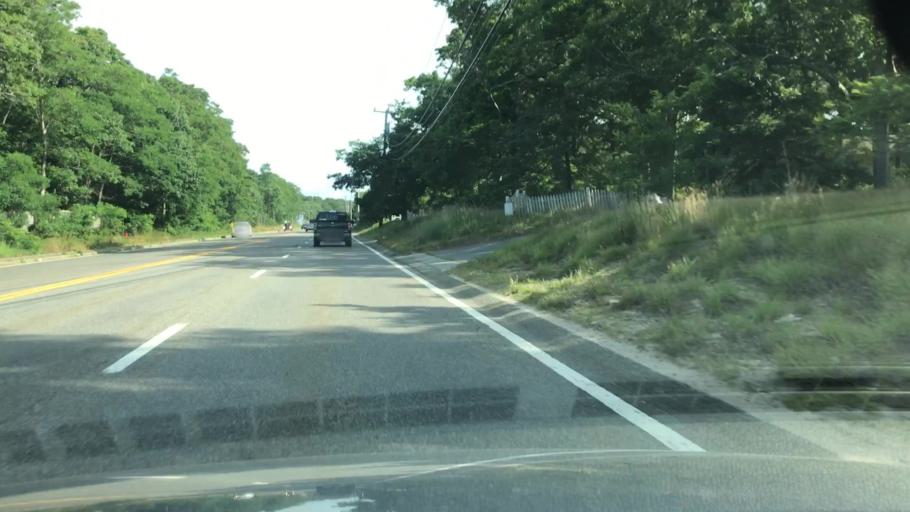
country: US
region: Massachusetts
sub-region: Barnstable County
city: North Eastham
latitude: 41.8743
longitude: -69.9868
